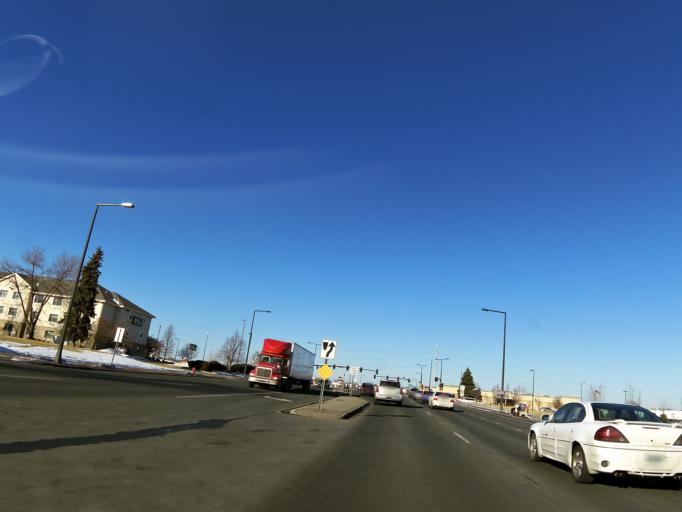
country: US
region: Minnesota
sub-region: Hennepin County
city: Bloomington
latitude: 44.8579
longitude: -93.2883
